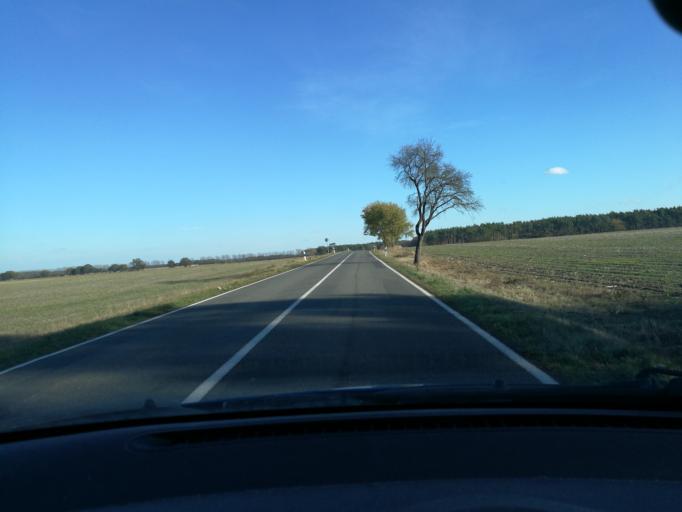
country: DE
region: Brandenburg
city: Lanz
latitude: 53.1653
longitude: 11.6426
